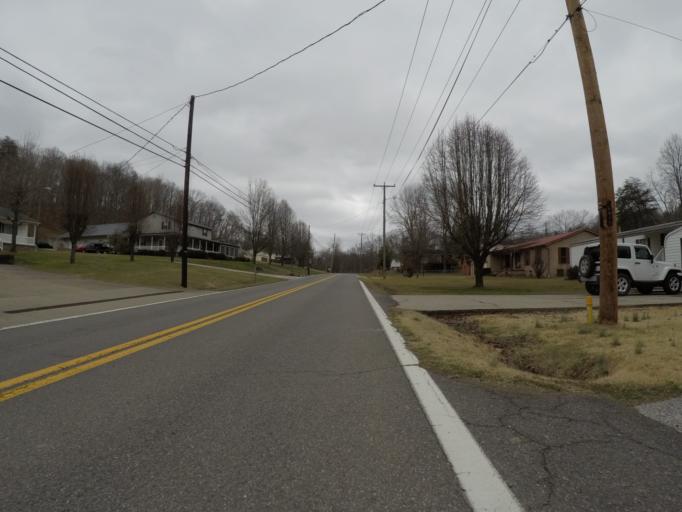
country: US
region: West Virginia
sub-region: Cabell County
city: Barboursville
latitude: 38.4434
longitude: -82.2973
